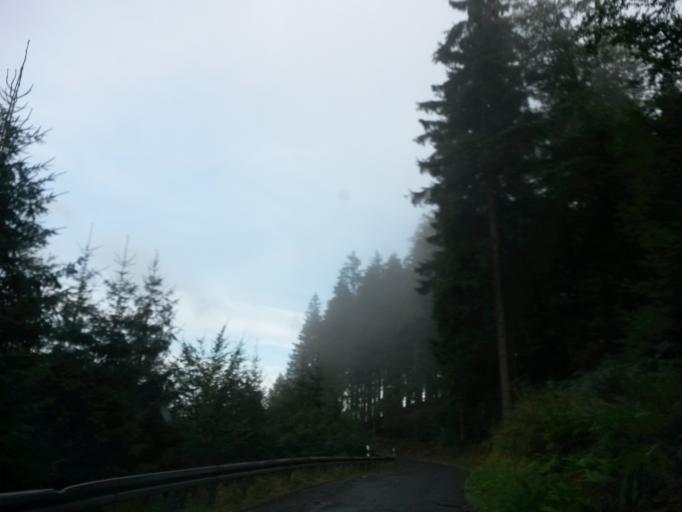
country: DE
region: North Rhine-Westphalia
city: Meinerzhagen
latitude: 51.0652
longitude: 7.6171
